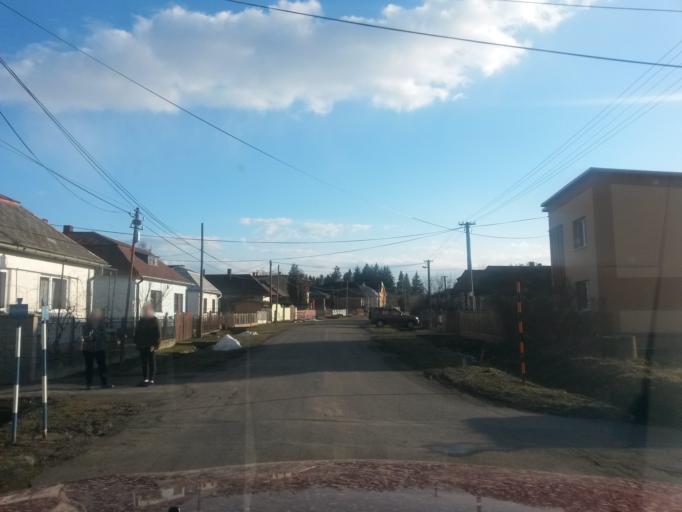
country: SK
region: Kosicky
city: Sobrance
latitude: 48.7744
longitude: 22.0847
